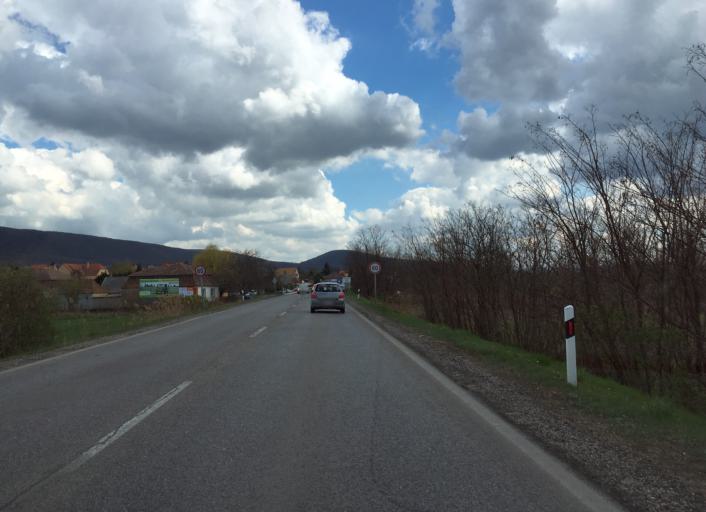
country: HU
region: Komarom-Esztergom
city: Vertesszolos
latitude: 47.6253
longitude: 18.3694
